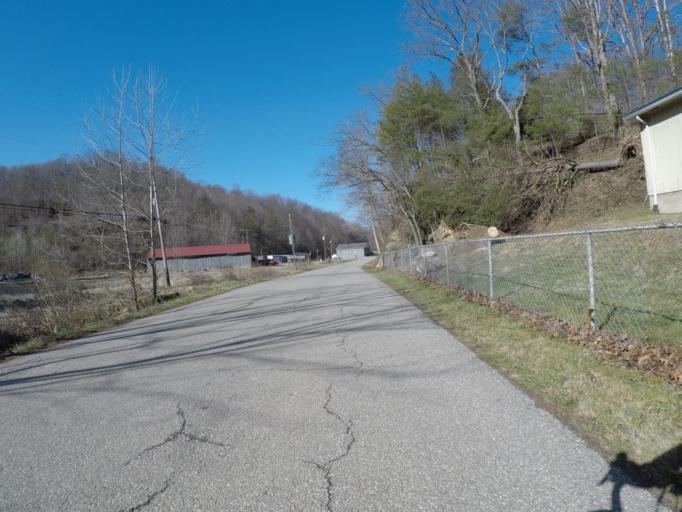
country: US
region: Kentucky
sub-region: Boyd County
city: Catlettsburg
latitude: 38.4103
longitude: -82.6389
